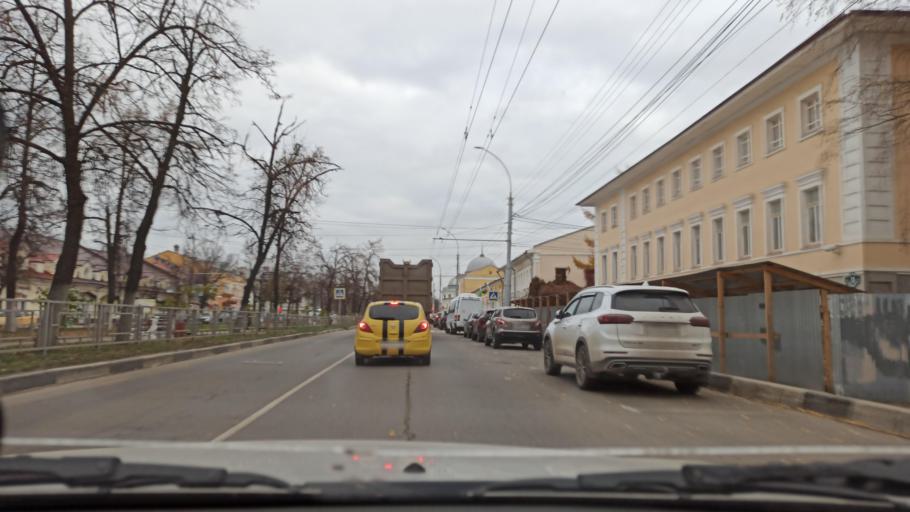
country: RU
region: Vologda
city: Vologda
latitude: 59.2198
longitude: 39.8870
